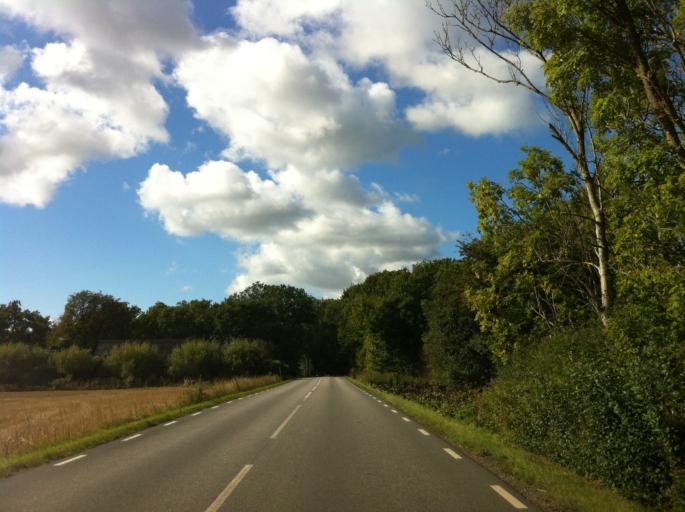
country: SE
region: Skane
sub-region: Tomelilla Kommun
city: Tomelilla
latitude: 55.6507
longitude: 13.9462
